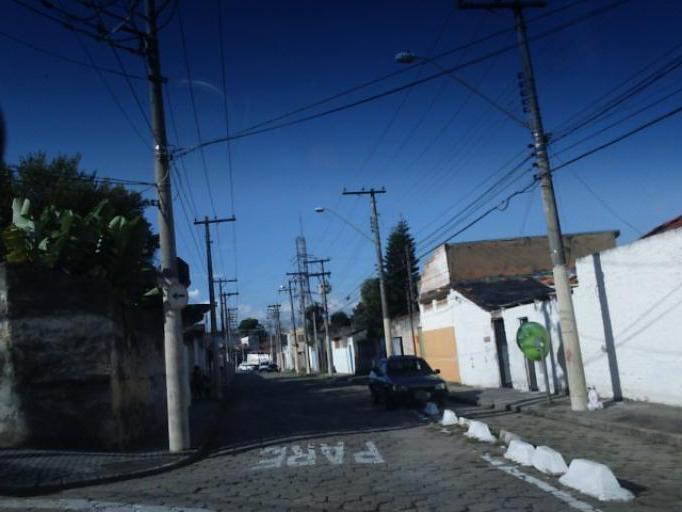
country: BR
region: Sao Paulo
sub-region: Sao Jose Dos Campos
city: Sao Jose dos Campos
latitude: -23.1899
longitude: -45.8840
